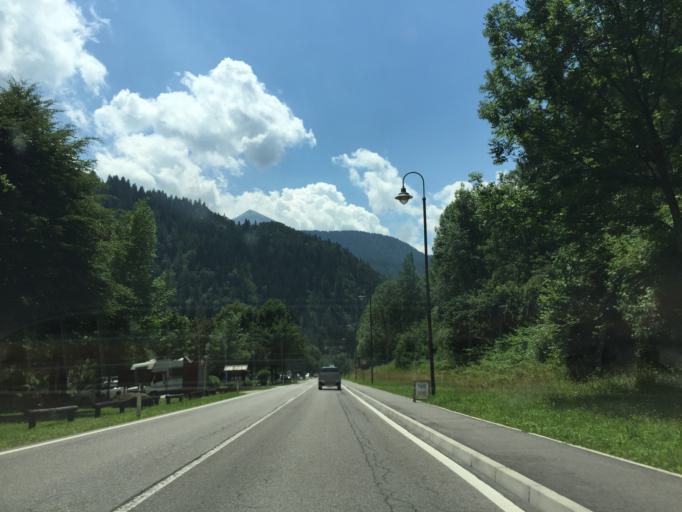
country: IT
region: Trentino-Alto Adige
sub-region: Provincia di Trento
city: Mezzano
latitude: 46.1631
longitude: 11.8209
